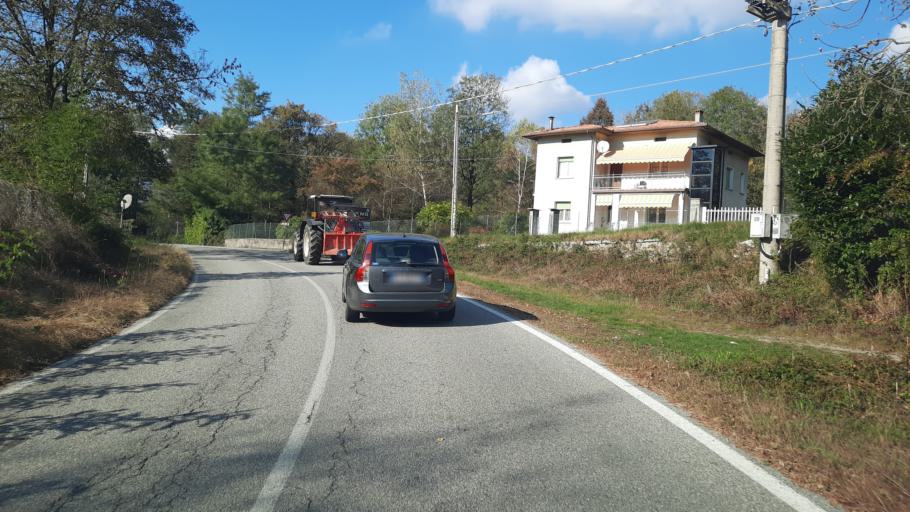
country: IT
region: Piedmont
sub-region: Provincia di Novara
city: Ameno
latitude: 45.7772
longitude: 8.4378
